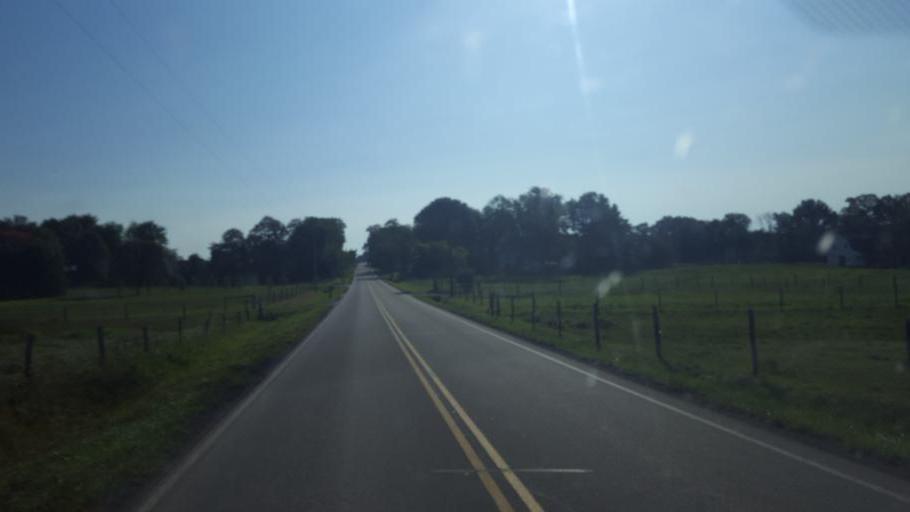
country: US
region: Ohio
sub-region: Portage County
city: Hiram
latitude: 41.3869
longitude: -81.1257
